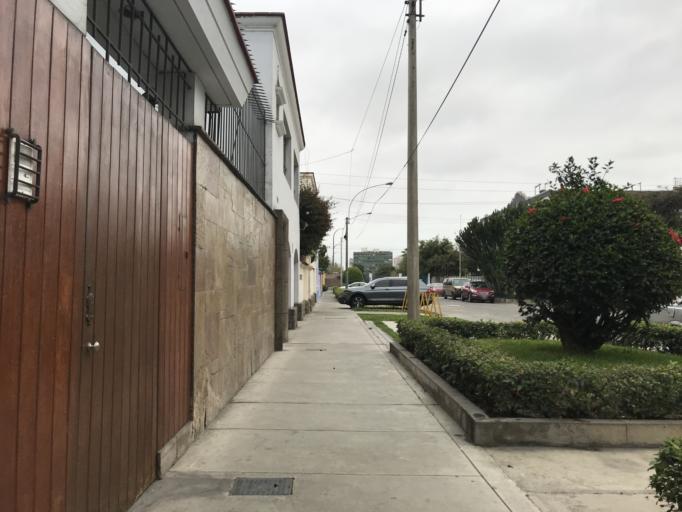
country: PE
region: Lima
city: Lima
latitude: -12.0762
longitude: -77.0381
